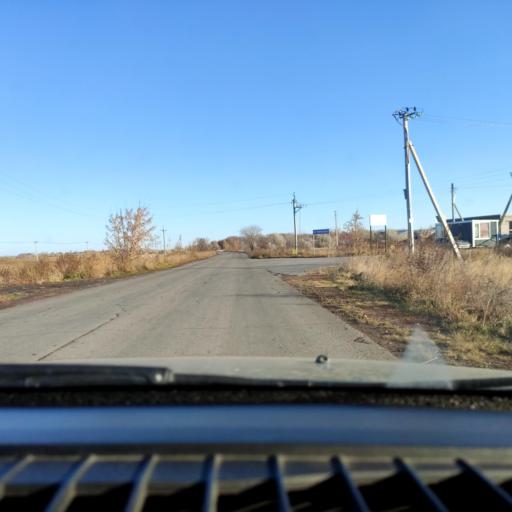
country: RU
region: Samara
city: Tol'yatti
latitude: 53.6445
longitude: 49.3171
